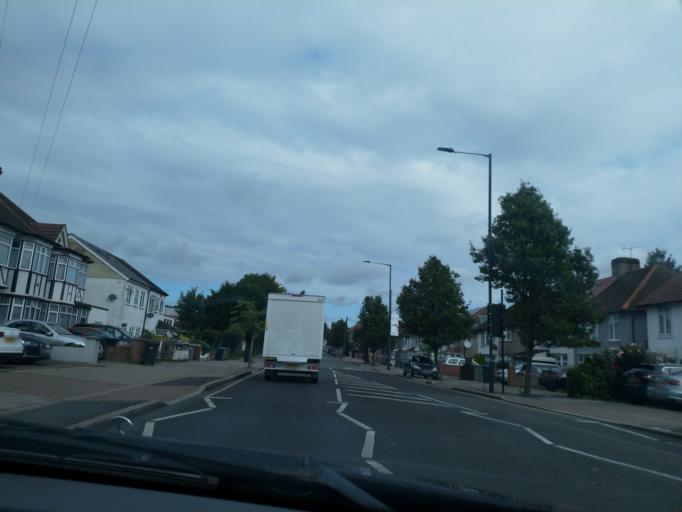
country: GB
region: England
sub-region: Greater London
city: Harrow on the Hill
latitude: 51.5584
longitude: -0.3183
